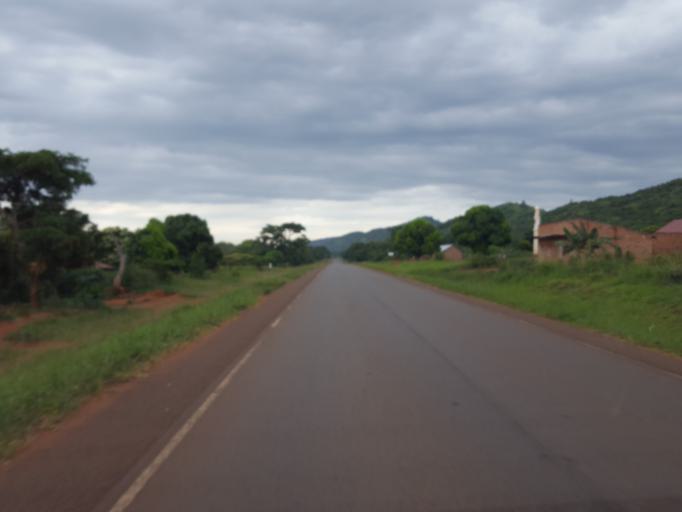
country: UG
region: Central Region
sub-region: Kiboga District
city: Kiboga
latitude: 0.8563
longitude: 31.8668
